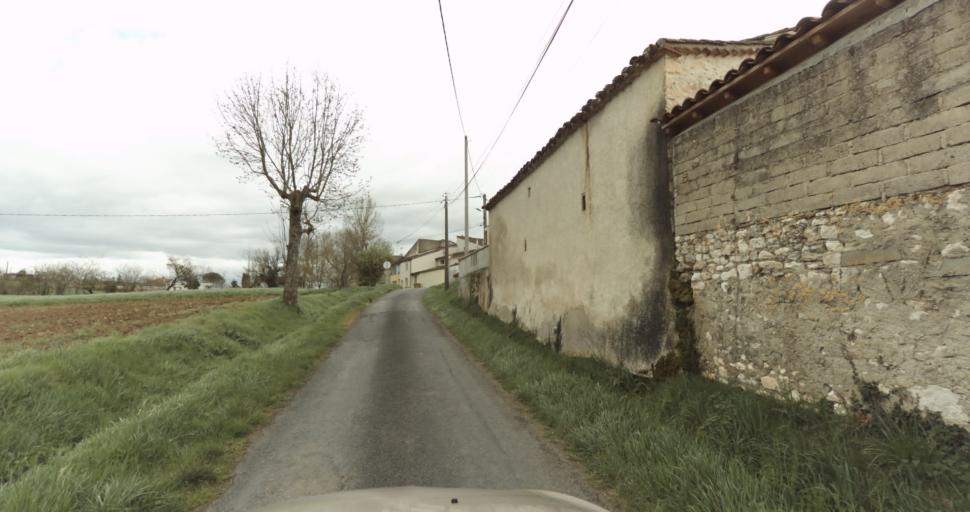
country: FR
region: Midi-Pyrenees
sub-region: Departement du Tarn
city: Puygouzon
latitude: 43.8955
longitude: 2.1604
